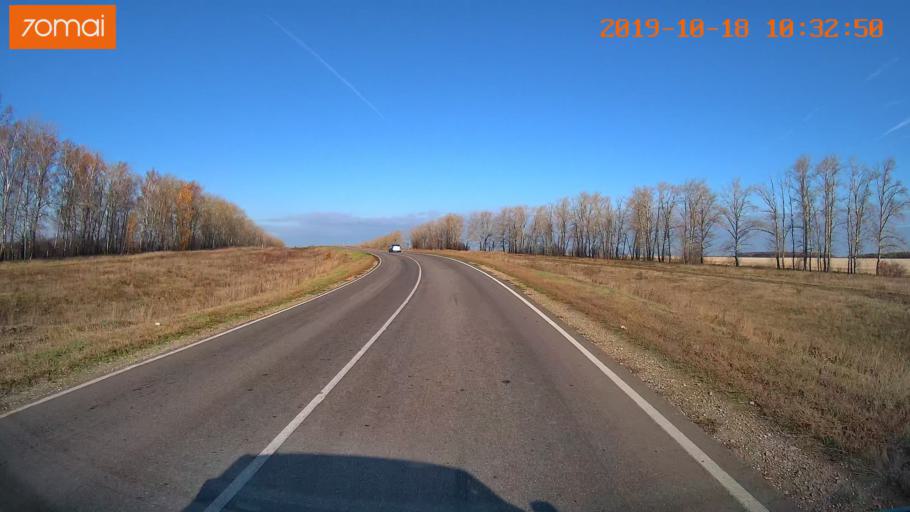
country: RU
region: Tula
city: Kurkino
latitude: 53.5001
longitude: 38.6205
